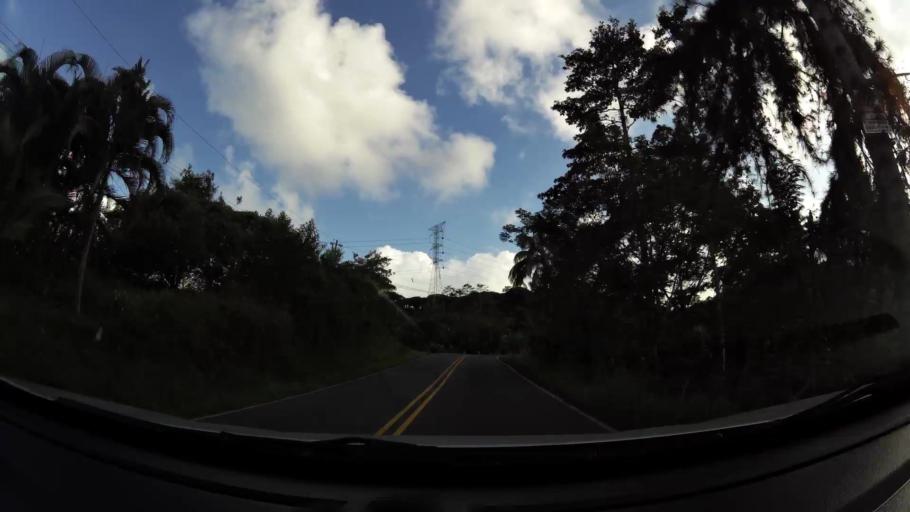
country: CR
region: Limon
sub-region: Canton de Siquirres
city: Siquirres
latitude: 10.0724
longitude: -83.5509
